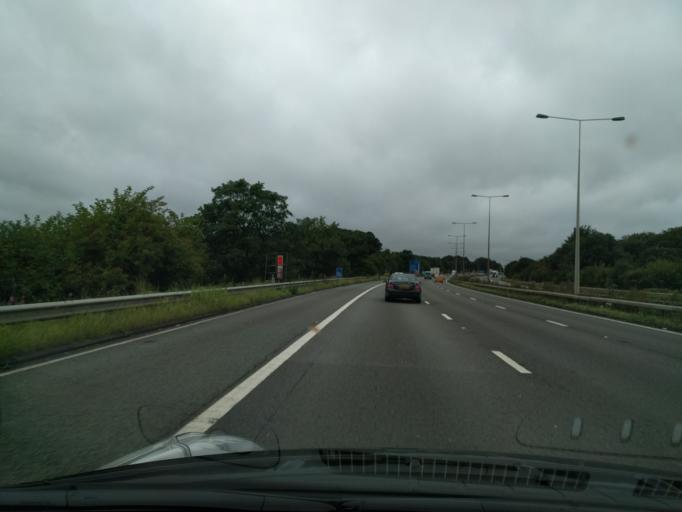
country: GB
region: England
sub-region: Borough of Wigan
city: Ashton in Makerfield
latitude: 53.4660
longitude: -2.6276
